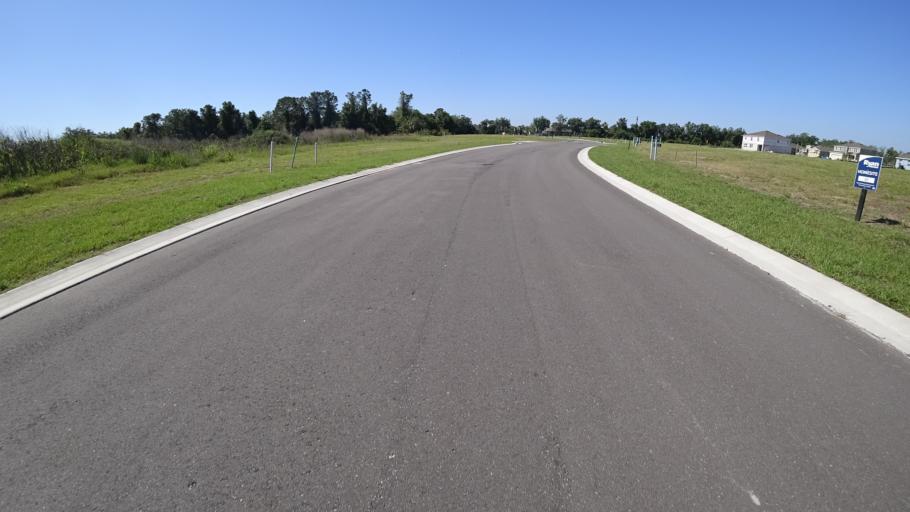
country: US
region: Florida
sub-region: Manatee County
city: Ellenton
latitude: 27.5702
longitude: -82.4420
